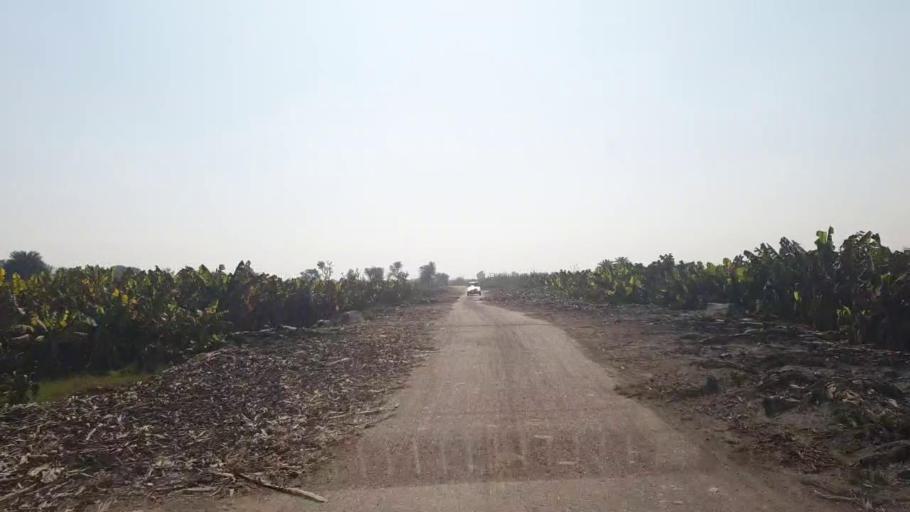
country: PK
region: Sindh
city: Sakrand
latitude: 26.0308
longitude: 68.4379
